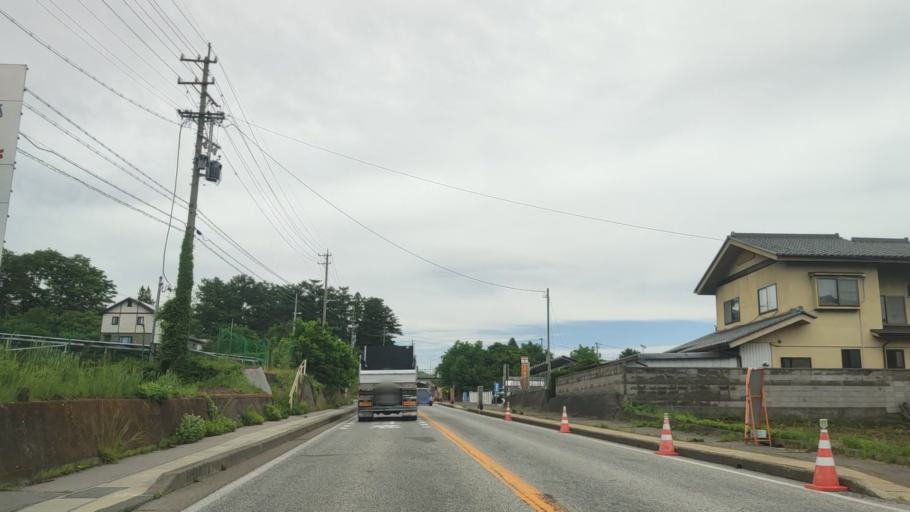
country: JP
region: Nagano
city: Komoro
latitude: 36.3434
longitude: 138.3847
